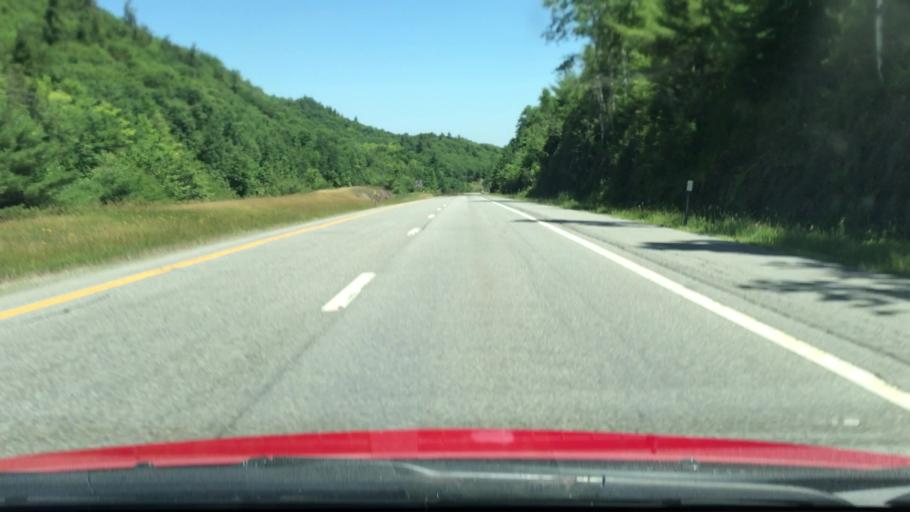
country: US
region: New York
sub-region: Essex County
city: Elizabethtown
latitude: 44.1860
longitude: -73.5660
